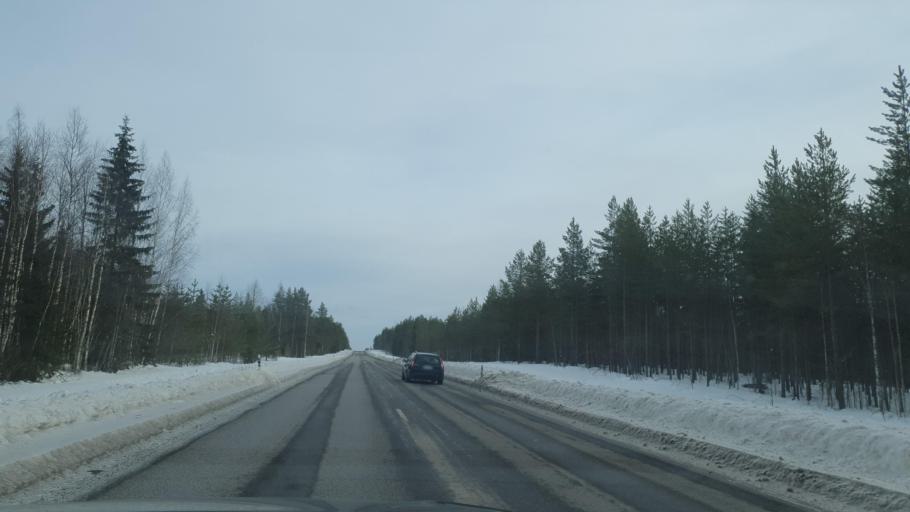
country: FI
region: Kainuu
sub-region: Kajaani
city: Vaala
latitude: 64.5522
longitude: 27.0562
